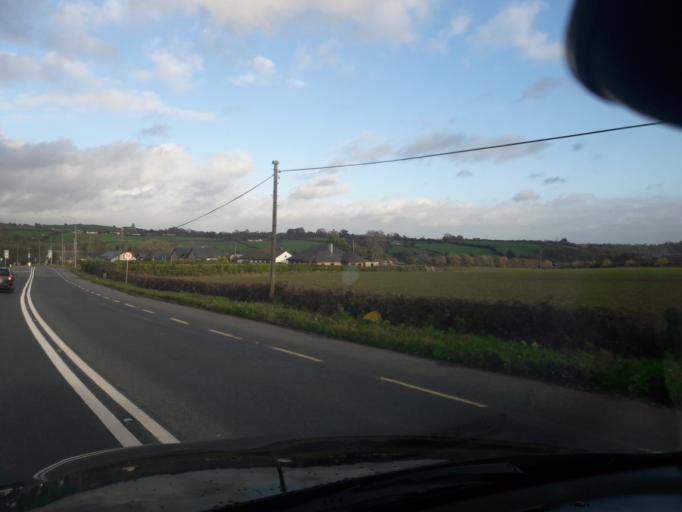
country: IE
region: Leinster
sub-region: An Mhi
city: Slane
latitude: 53.6966
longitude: -6.5390
